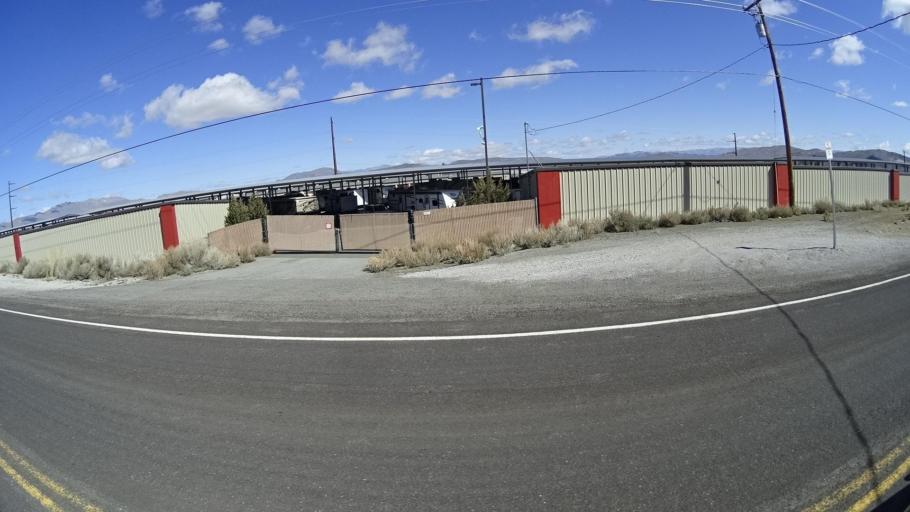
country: US
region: Nevada
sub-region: Washoe County
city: Lemmon Valley
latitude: 39.6180
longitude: -119.8874
